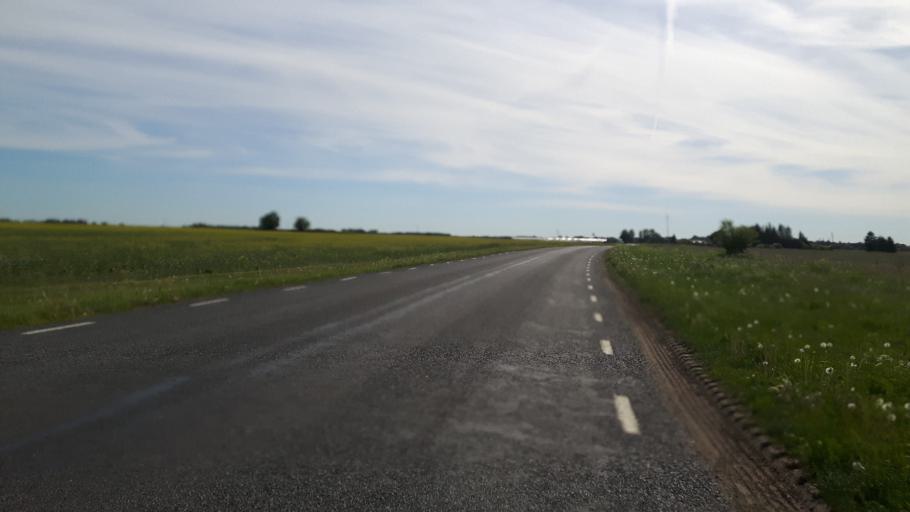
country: EE
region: Harju
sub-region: Raasiku vald
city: Arukula
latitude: 59.4363
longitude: 25.1254
